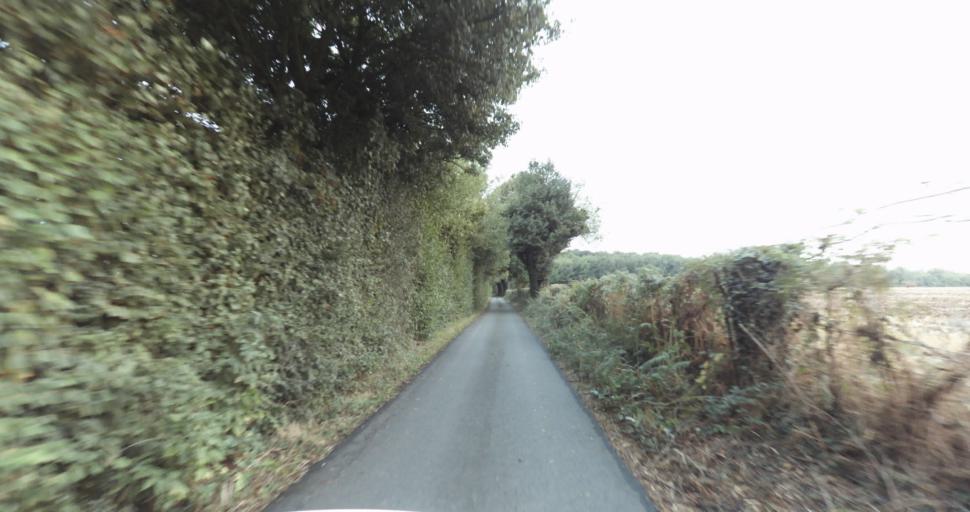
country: FR
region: Lower Normandy
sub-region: Departement de l'Orne
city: Vimoutiers
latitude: 48.9117
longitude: 0.1168
